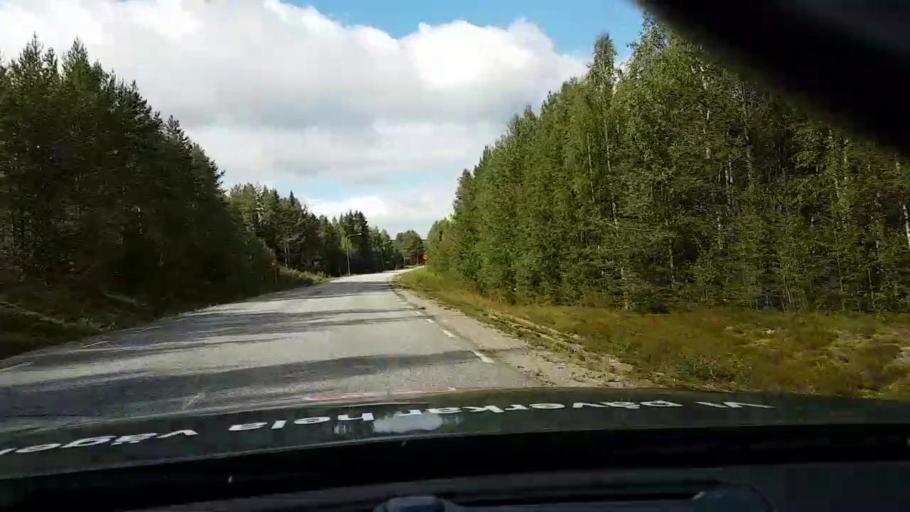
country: SE
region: Vaesterbotten
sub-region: Asele Kommun
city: Asele
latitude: 63.9327
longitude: 17.2925
